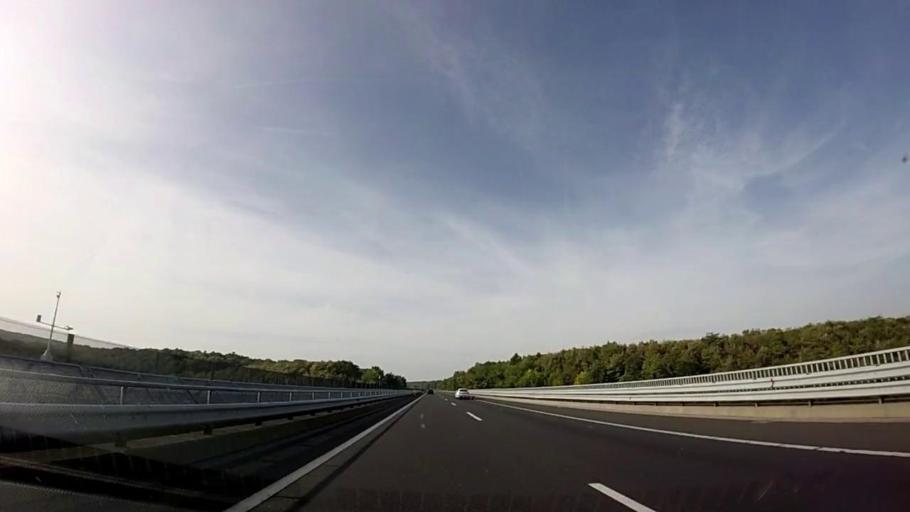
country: HU
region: Somogy
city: Zamardi
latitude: 46.8324
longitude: 17.9425
